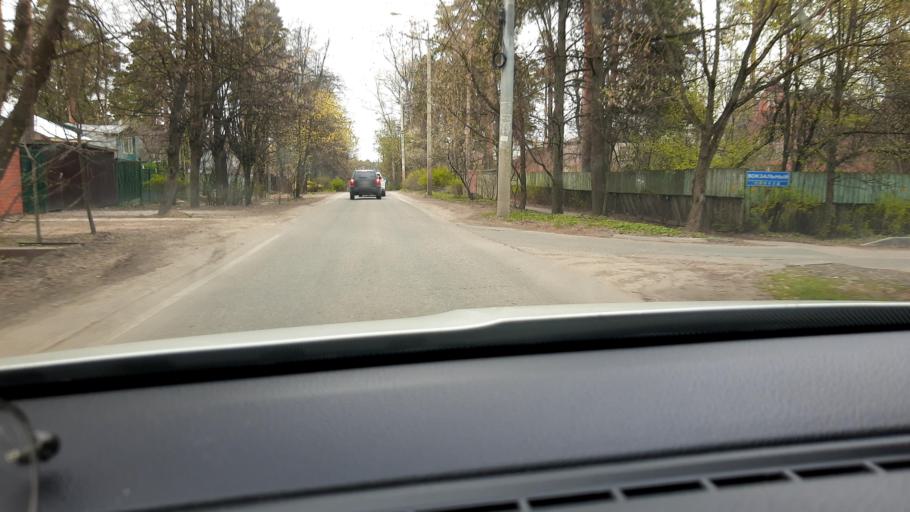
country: RU
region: Moskovskaya
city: Vidnoye
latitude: 55.5466
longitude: 37.6802
